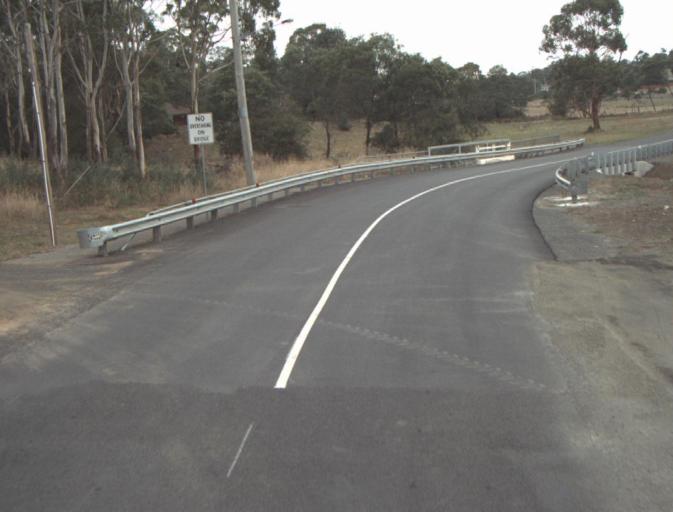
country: AU
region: Tasmania
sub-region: Launceston
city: Summerhill
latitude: -41.4939
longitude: 147.1812
